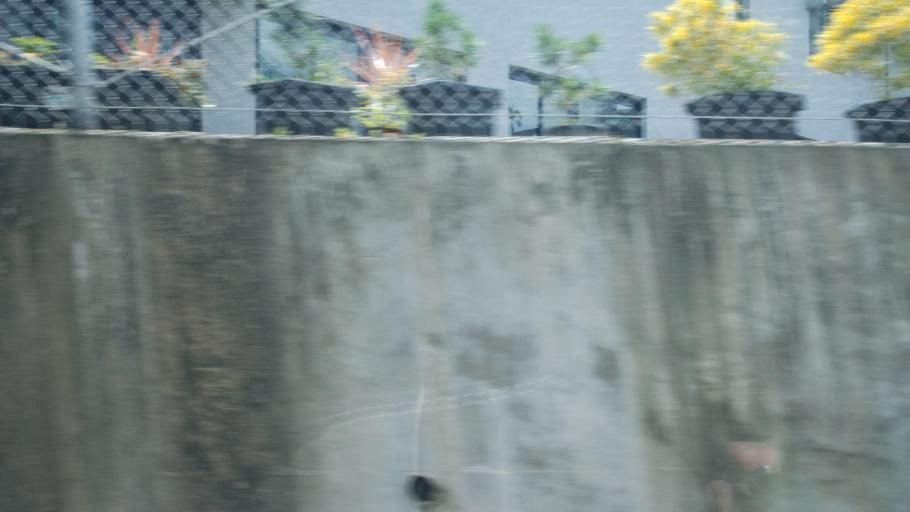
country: TW
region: Taipei
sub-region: Taipei
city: Banqiao
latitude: 24.9493
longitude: 121.4926
